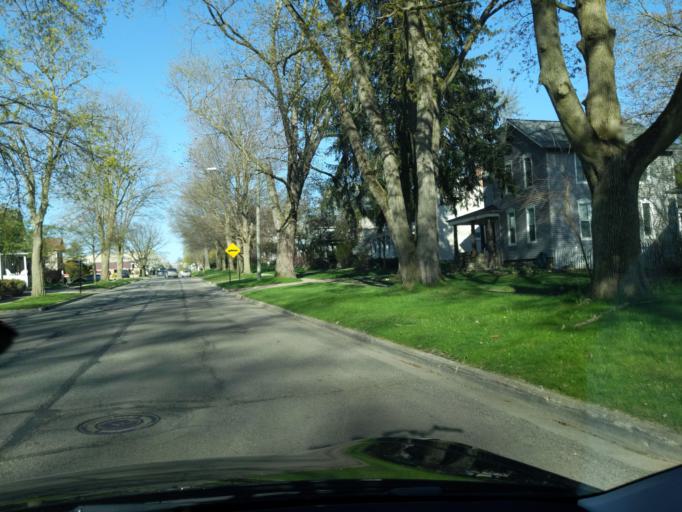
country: US
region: Michigan
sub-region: Washtenaw County
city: Chelsea
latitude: 42.3171
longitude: -84.0242
